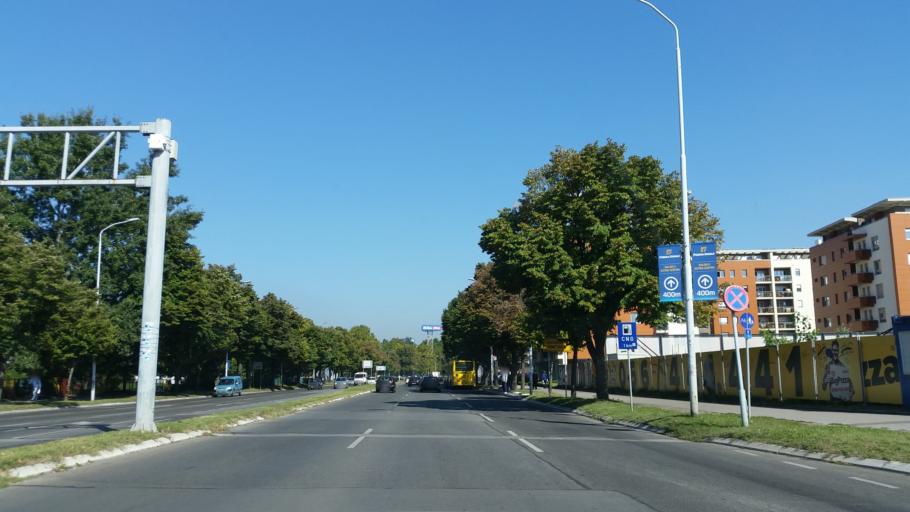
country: RS
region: Central Serbia
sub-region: Belgrade
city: Novi Beograd
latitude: 44.8048
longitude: 20.3995
